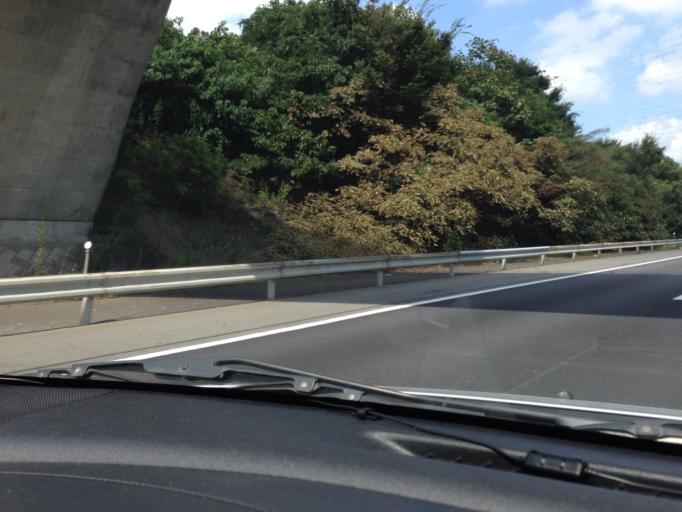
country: JP
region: Ibaraki
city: Naka
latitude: 36.1096
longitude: 140.1782
